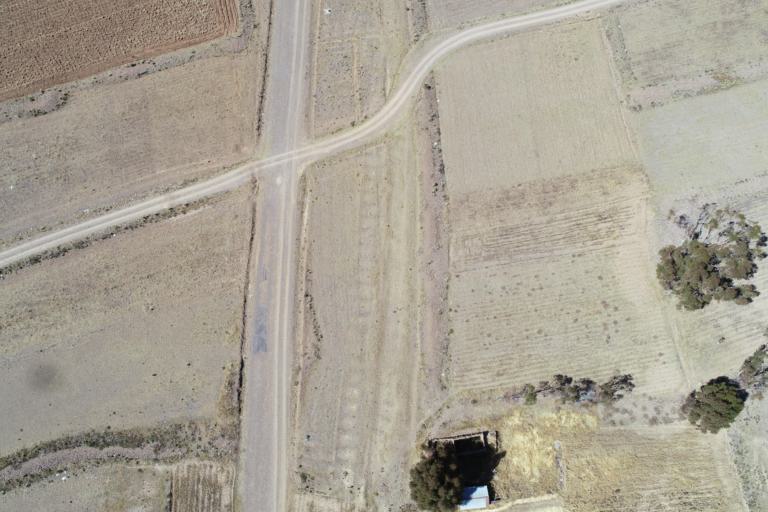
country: BO
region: La Paz
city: Achacachi
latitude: -15.9013
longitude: -68.9019
